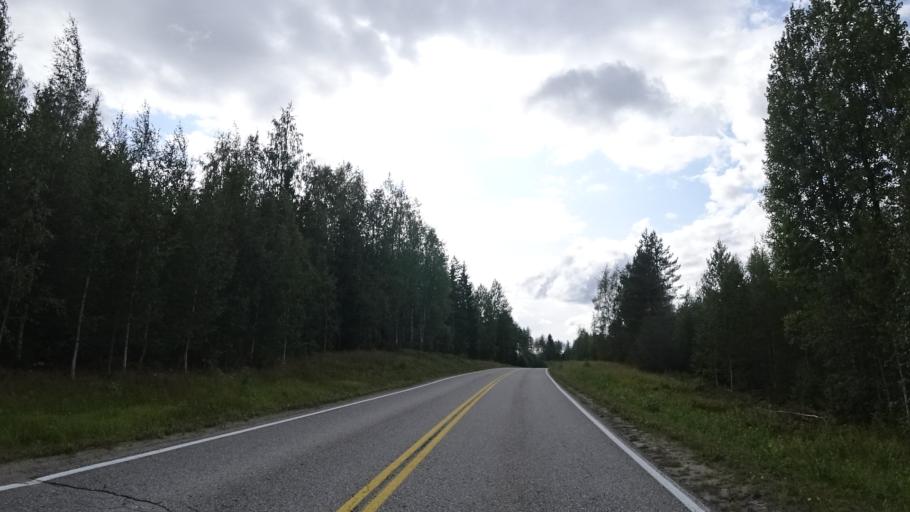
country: FI
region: North Karelia
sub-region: Joensuu
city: Ilomantsi
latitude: 62.7716
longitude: 31.0643
